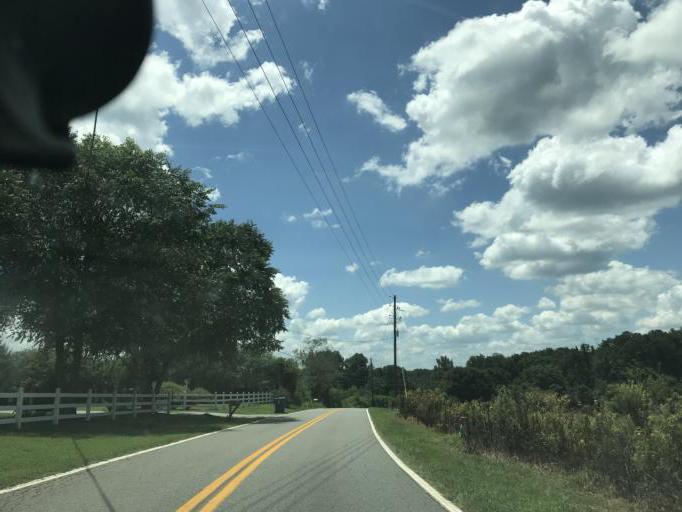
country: US
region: Georgia
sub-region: Fulton County
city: Milton
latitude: 34.2219
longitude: -84.2541
